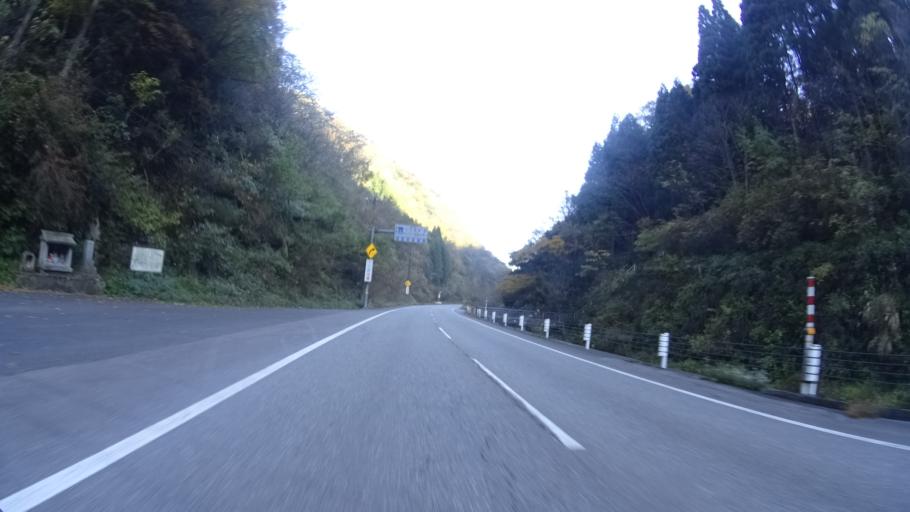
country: JP
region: Fukui
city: Maruoka
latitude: 36.1898
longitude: 136.3432
